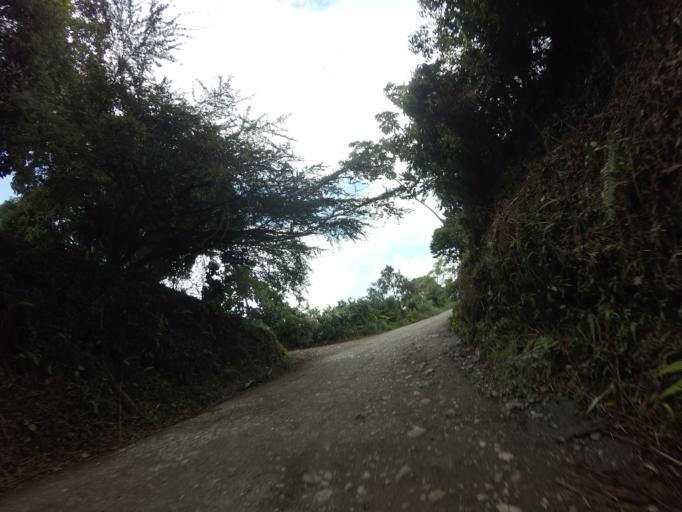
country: CO
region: Caldas
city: Victoria
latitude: 5.3230
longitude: -74.9400
